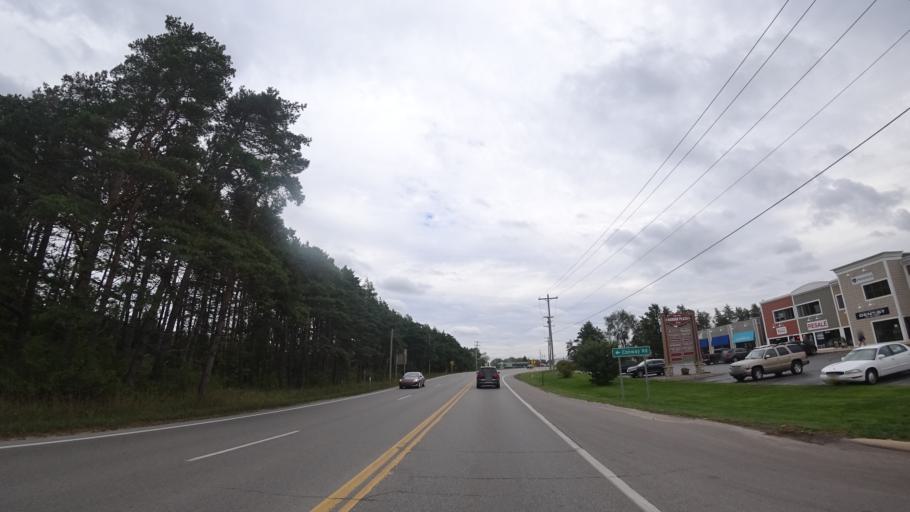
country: US
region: Michigan
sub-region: Emmet County
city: Petoskey
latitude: 45.4279
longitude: -84.9082
